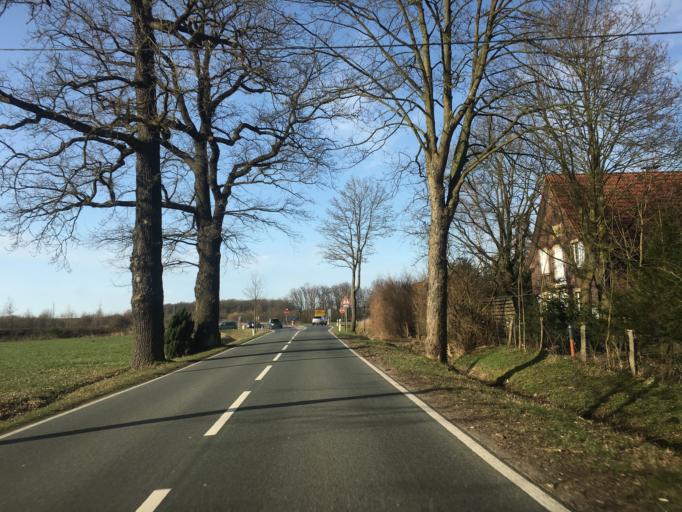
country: DE
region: North Rhine-Westphalia
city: Olfen
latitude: 51.7006
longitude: 7.4141
